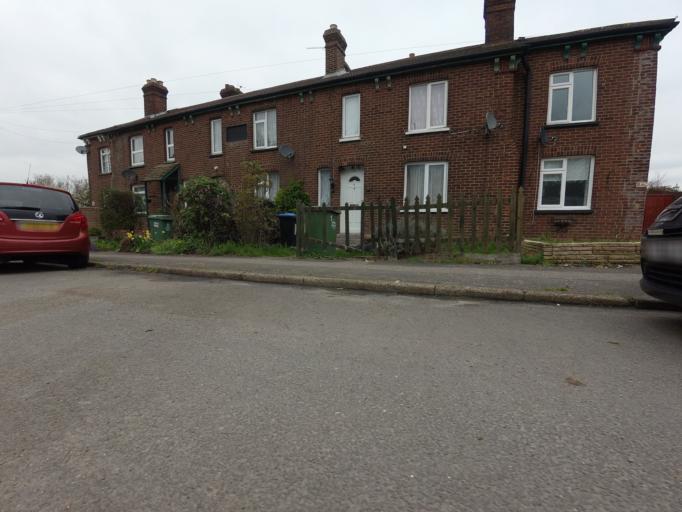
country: GB
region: England
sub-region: Kent
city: Swanley
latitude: 51.4098
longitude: 0.1453
